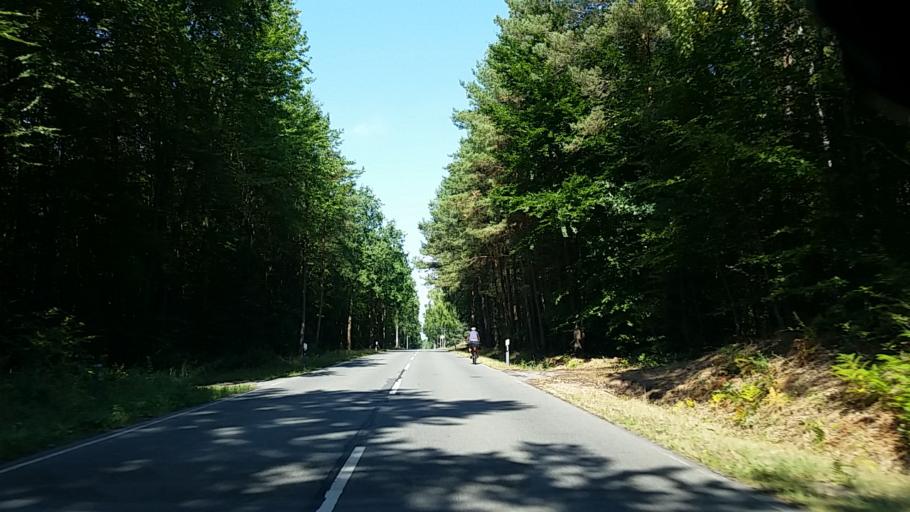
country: DE
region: Lower Saxony
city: Jelmstorf
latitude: 53.1169
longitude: 10.5433
